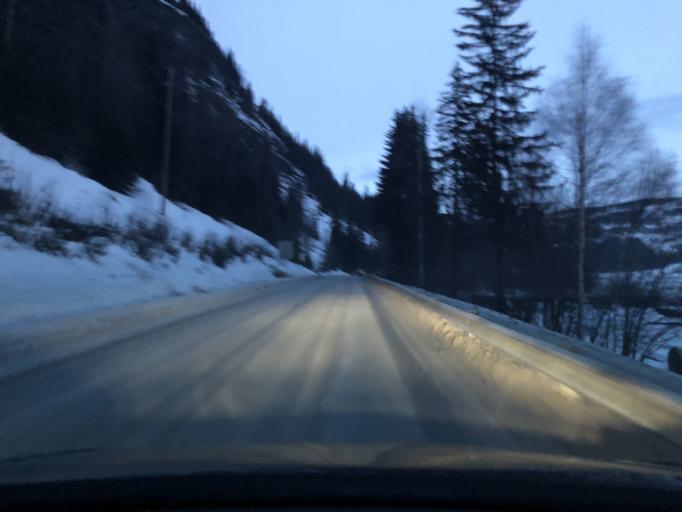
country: NO
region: Oppland
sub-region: Nord-Aurdal
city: Fagernes
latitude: 61.0001
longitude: 9.2099
